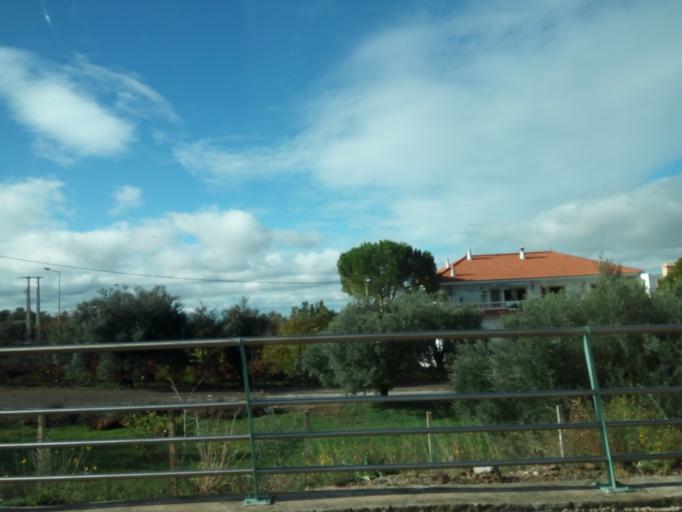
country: PT
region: Faro
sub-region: Loule
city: Loule
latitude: 37.1302
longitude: -8.0050
